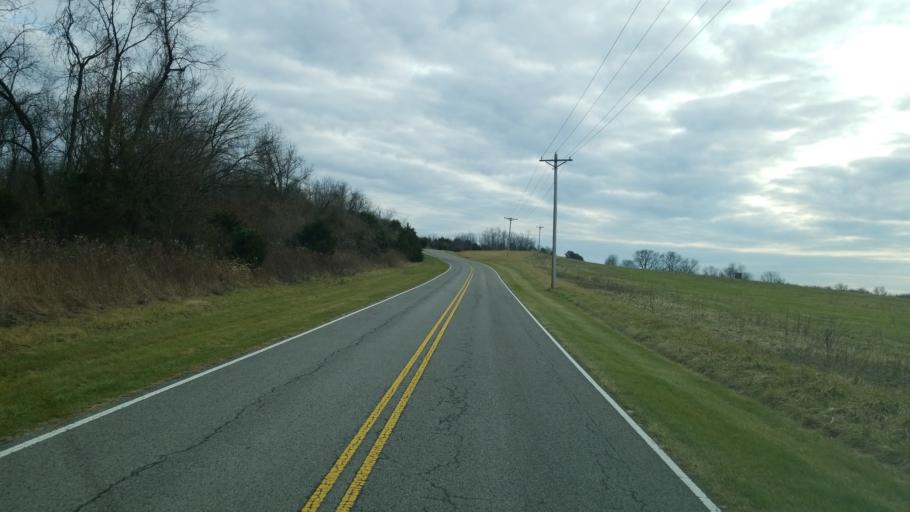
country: US
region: Ohio
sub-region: Highland County
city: Greenfield
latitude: 39.2346
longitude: -83.3888
